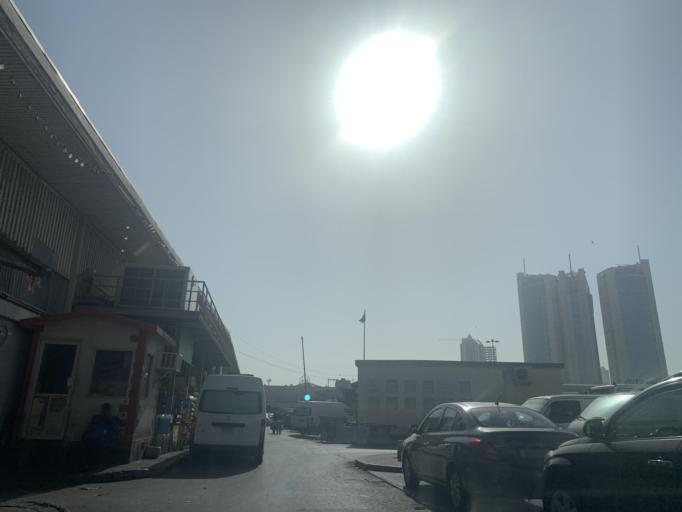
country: BH
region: Manama
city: Jidd Hafs
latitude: 26.2306
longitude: 50.5657
